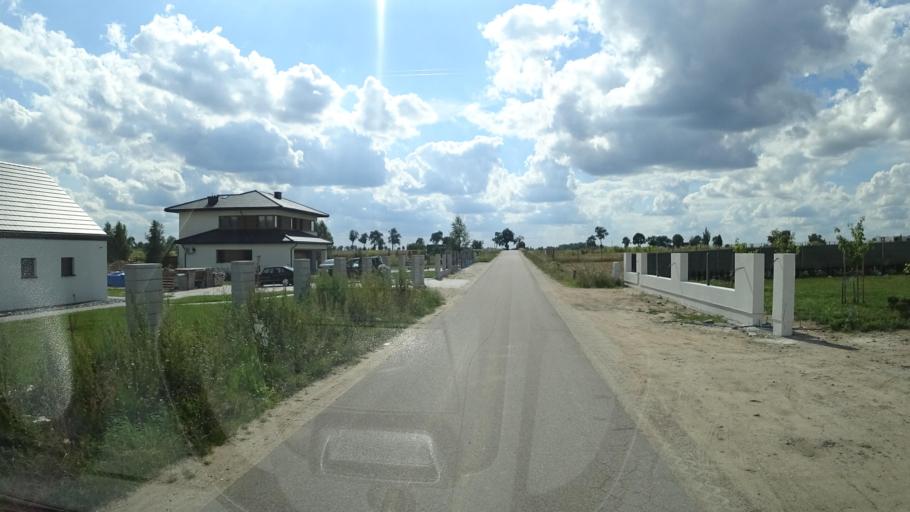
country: PL
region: Podlasie
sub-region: Powiat lomzynski
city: Piatnica
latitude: 53.1393
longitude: 22.1194
